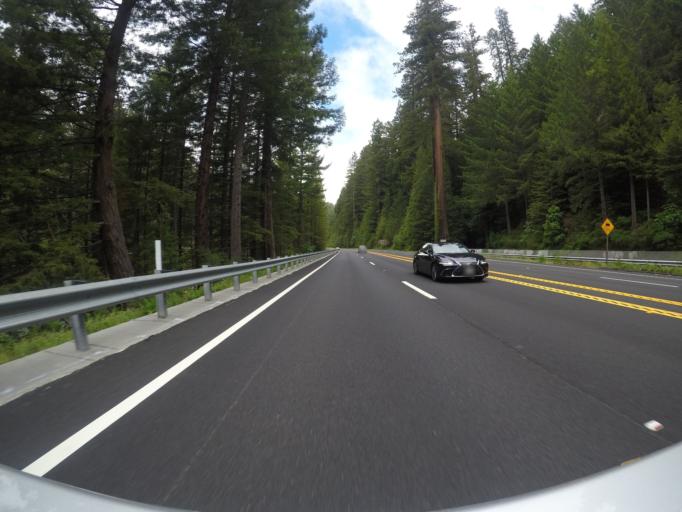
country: US
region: California
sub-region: Humboldt County
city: Rio Dell
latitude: 40.3471
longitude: -123.9307
